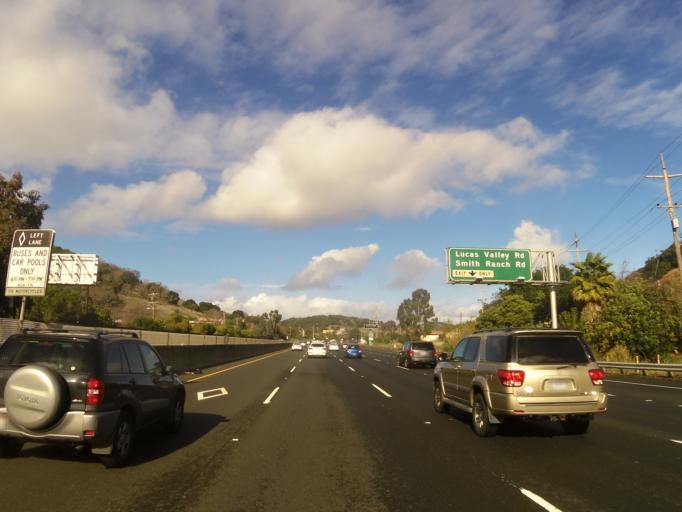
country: US
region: California
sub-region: Marin County
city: Santa Venetia
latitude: 38.0102
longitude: -122.5420
